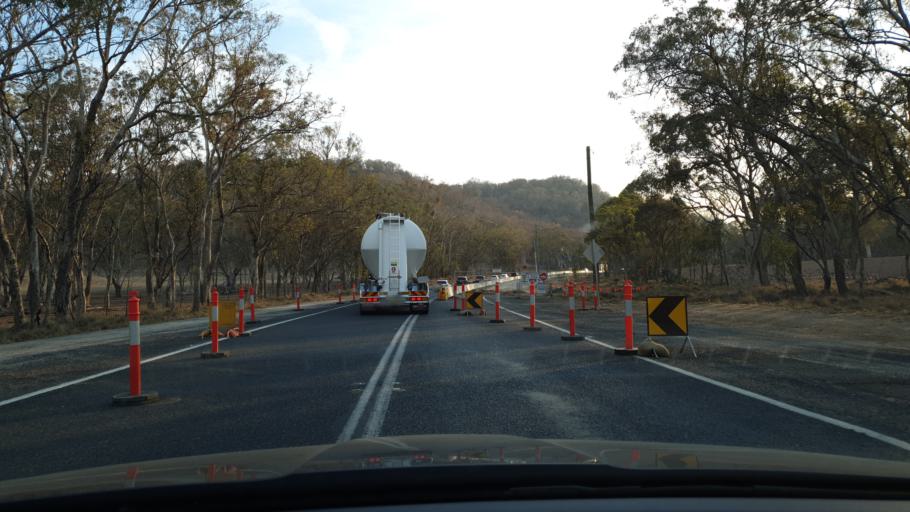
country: AU
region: New South Wales
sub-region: Glen Innes Severn
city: Glen Innes
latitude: -29.3112
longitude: 151.9347
